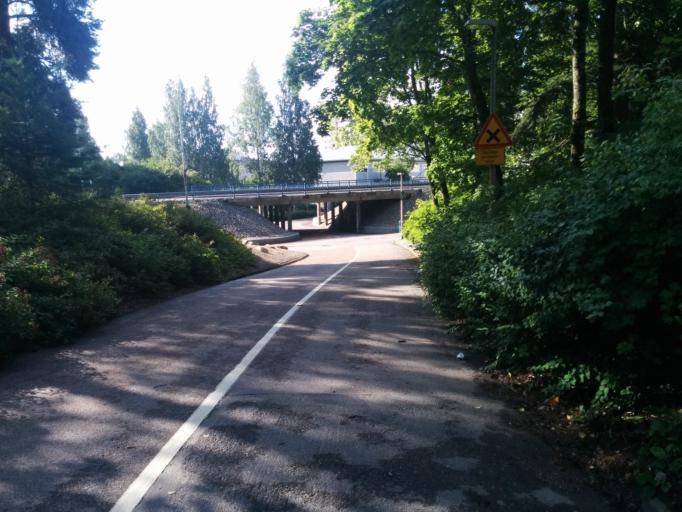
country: FI
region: Uusimaa
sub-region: Helsinki
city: Kerava
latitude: 60.4069
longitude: 25.0987
